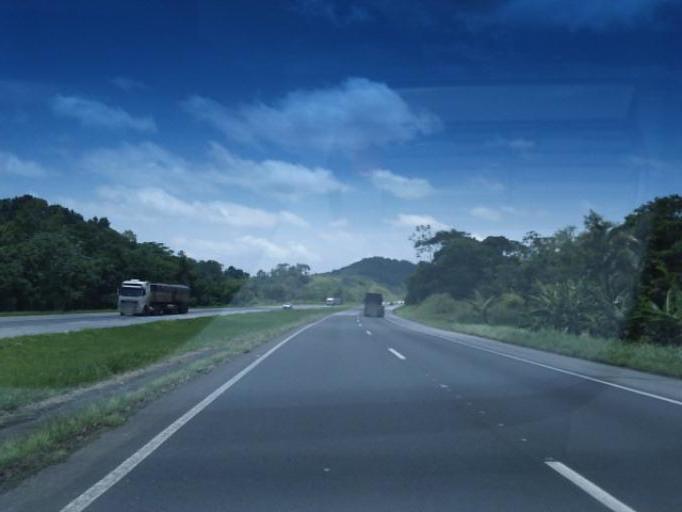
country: BR
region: Sao Paulo
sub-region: Juquia
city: Juquia
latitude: -24.3694
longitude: -47.6980
